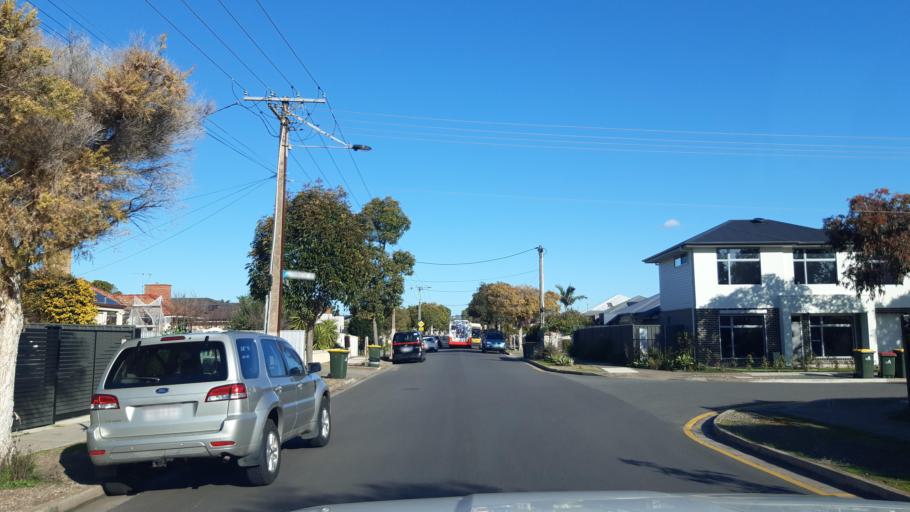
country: AU
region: South Australia
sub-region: Marion
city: Clovelly Park
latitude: -34.9950
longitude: 138.5672
